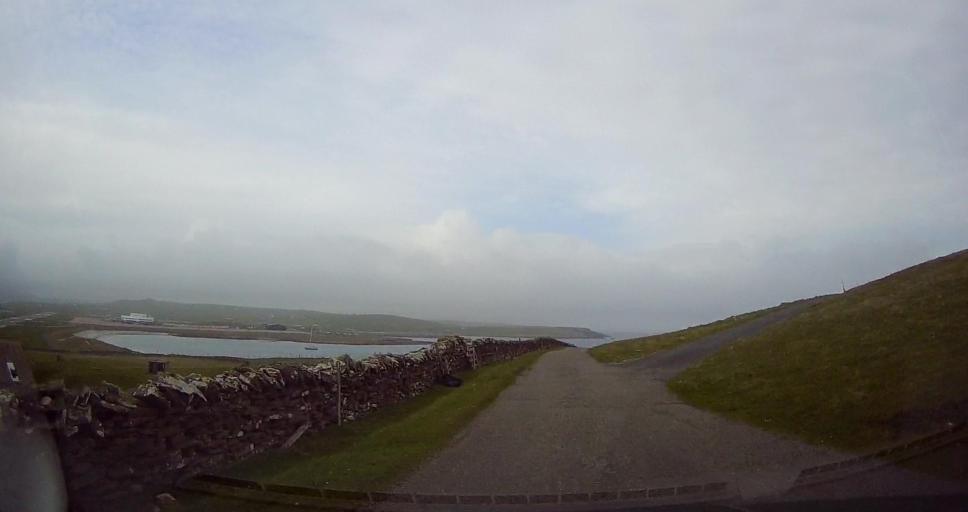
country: GB
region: Scotland
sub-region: Shetland Islands
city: Sandwick
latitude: 59.8690
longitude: -1.2791
